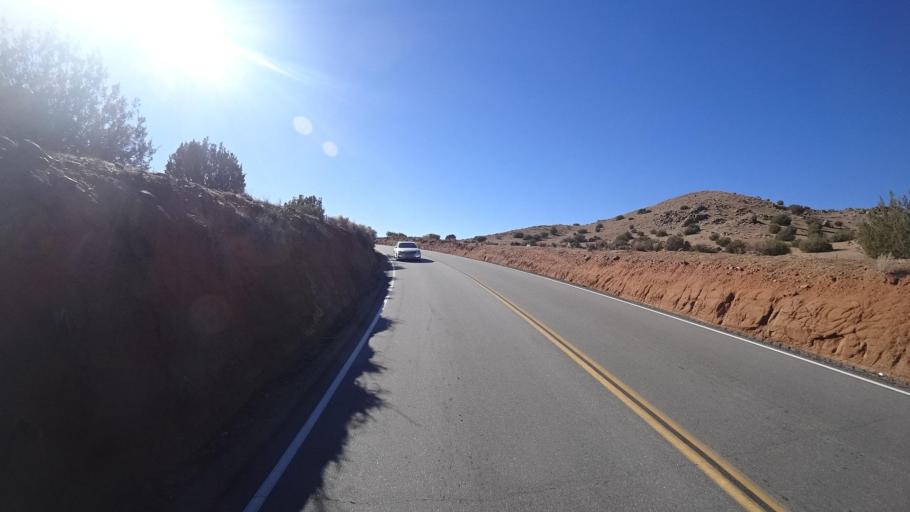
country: US
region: California
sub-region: Kern County
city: Wofford Heights
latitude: 35.6836
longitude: -118.3854
